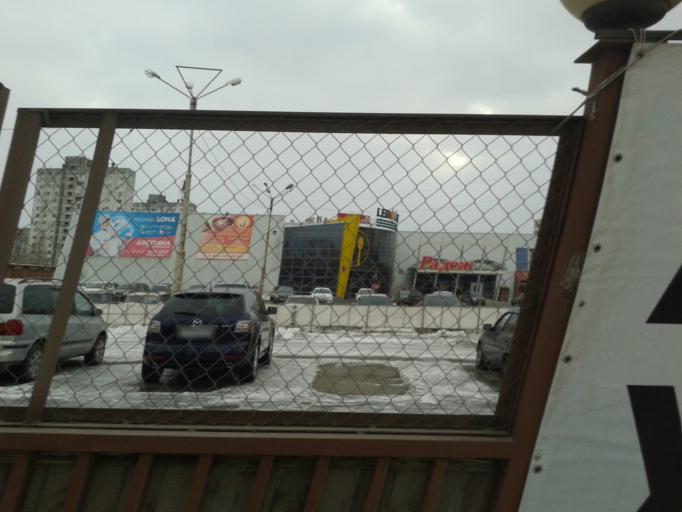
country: RU
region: Volgograd
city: Volgograd
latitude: 48.7242
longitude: 44.5152
